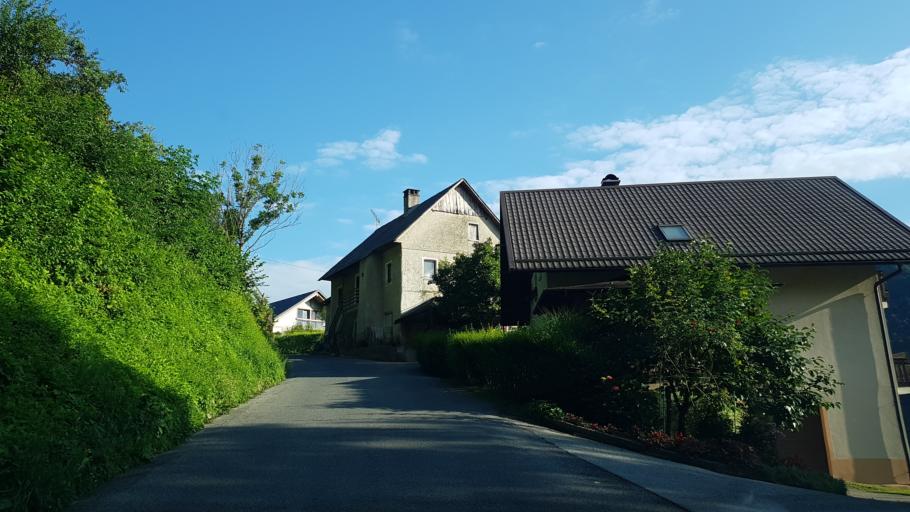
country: SI
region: Cerkno
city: Cerkno
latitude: 46.0876
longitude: 13.9739
